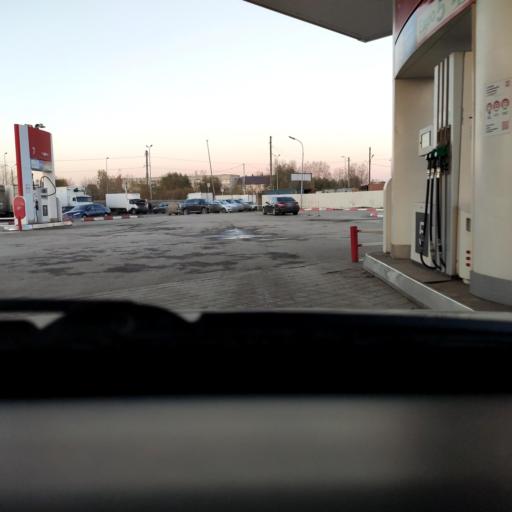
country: RU
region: Perm
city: Kondratovo
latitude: 57.9995
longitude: 56.1167
